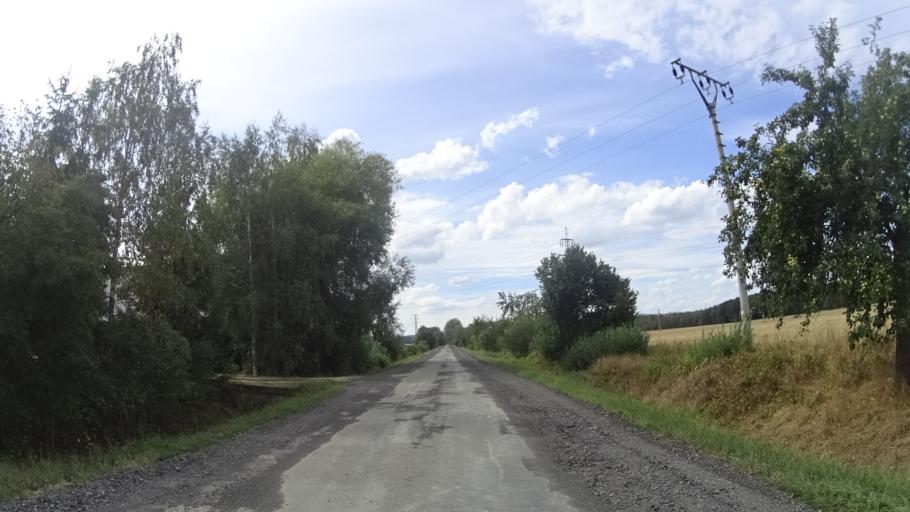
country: CZ
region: Olomoucky
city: Cervenka
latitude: 49.7138
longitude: 17.0560
